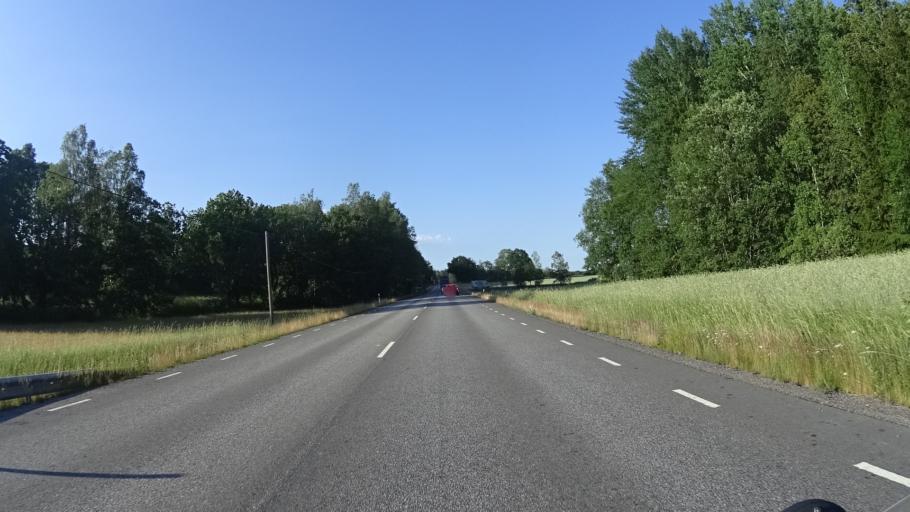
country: SE
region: Stockholm
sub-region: Sodertalje Kommun
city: Pershagen
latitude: 59.0949
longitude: 17.6198
